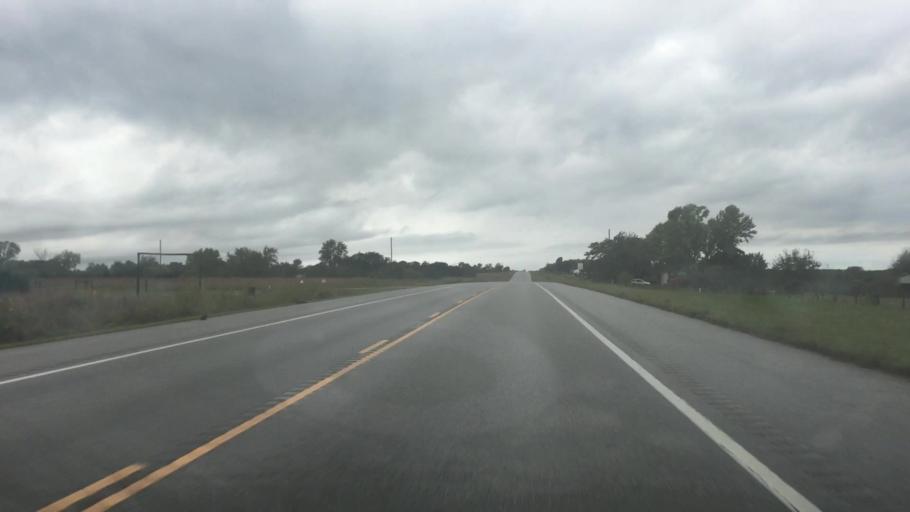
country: US
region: Kansas
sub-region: Miami County
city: Osawatomie
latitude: 38.4394
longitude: -94.9997
